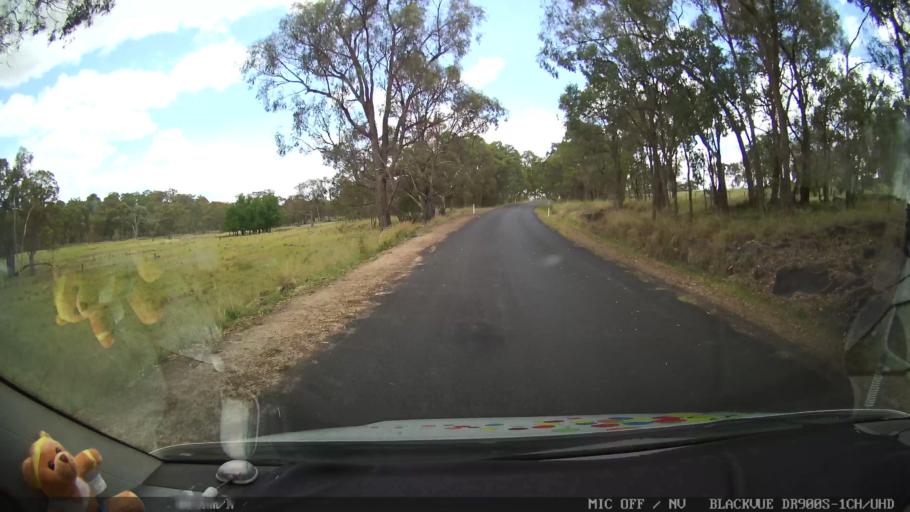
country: AU
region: New South Wales
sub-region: Glen Innes Severn
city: Glen Innes
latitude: -29.4286
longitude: 151.6613
